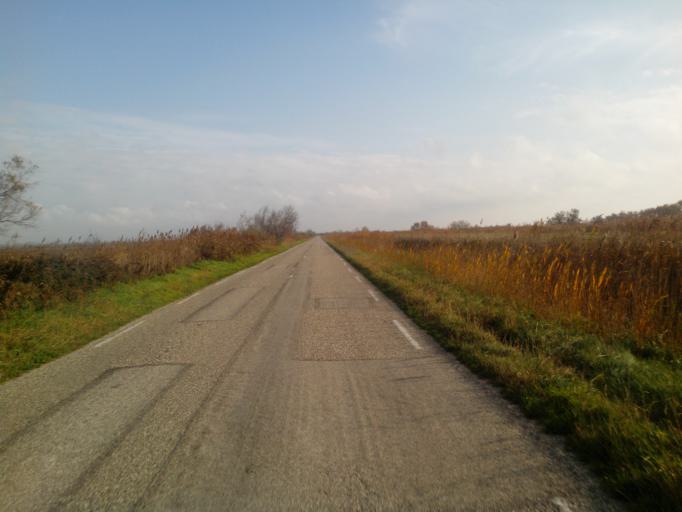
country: FR
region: Languedoc-Roussillon
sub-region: Departement du Gard
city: Saint-Gilles
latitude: 43.5790
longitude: 4.5155
